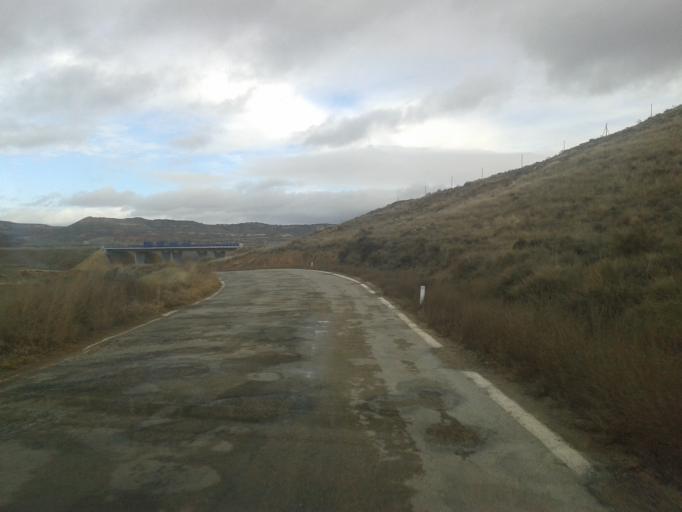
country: ES
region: Aragon
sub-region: Provincia de Teruel
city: Calamocha
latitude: 40.9236
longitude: -1.2684
